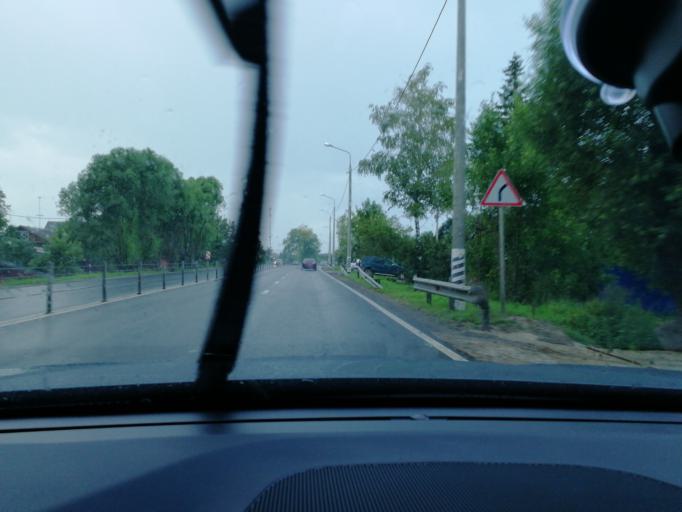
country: RU
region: Moskovskaya
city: Klimovsk
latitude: 55.3464
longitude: 37.5282
